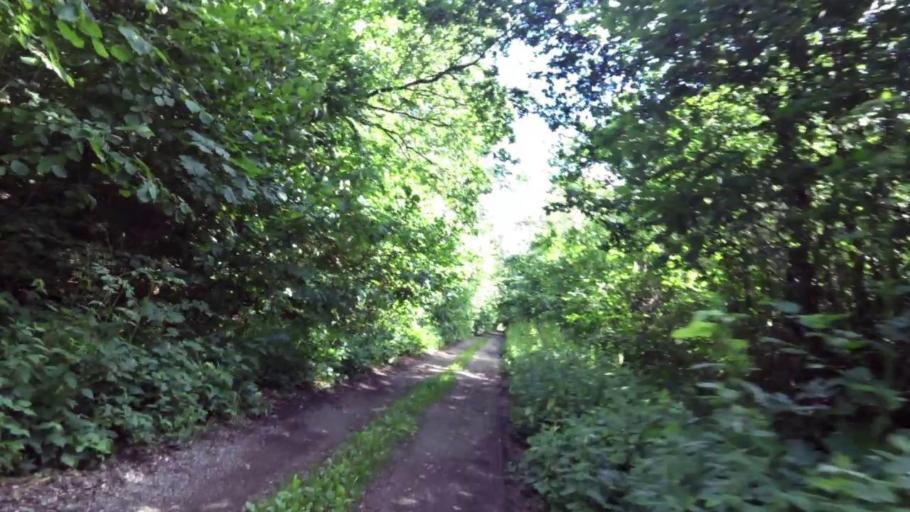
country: PL
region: West Pomeranian Voivodeship
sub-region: Powiat slawienski
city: Slawno
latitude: 54.5051
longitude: 16.7045
